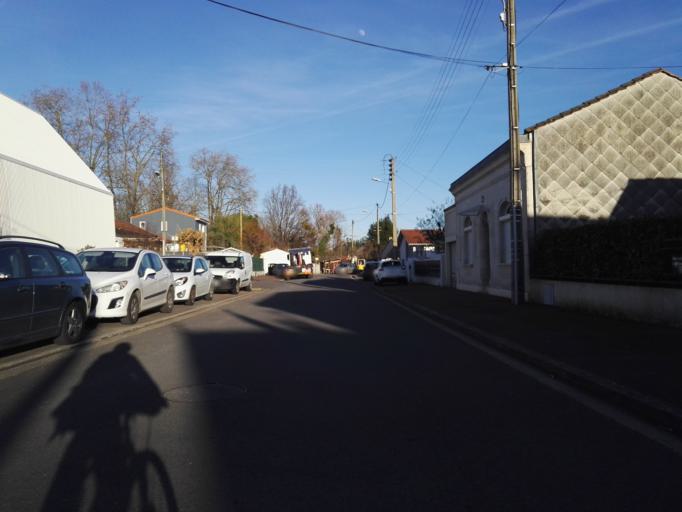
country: FR
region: Aquitaine
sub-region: Departement de la Gironde
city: Merignac
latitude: 44.8204
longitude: -0.6149
